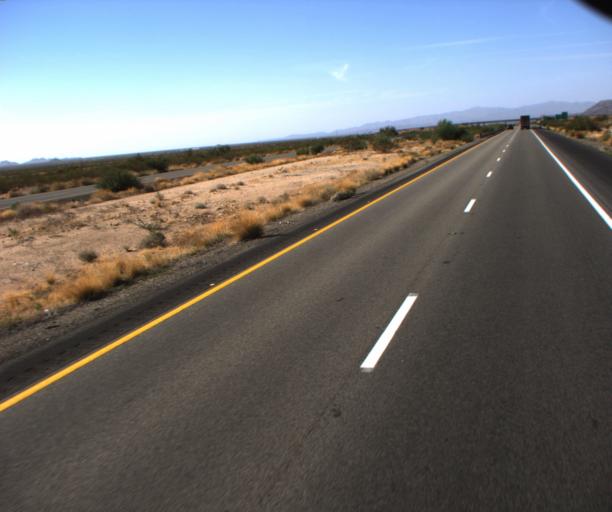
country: US
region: Arizona
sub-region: Mohave County
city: Kingman
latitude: 34.9212
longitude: -114.1515
